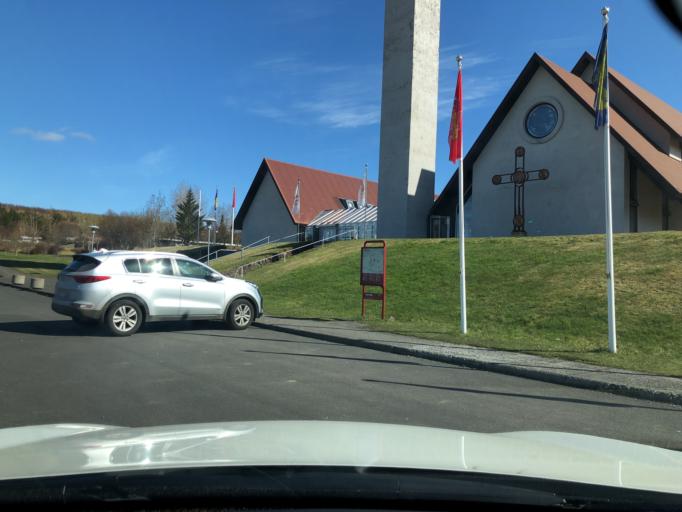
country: IS
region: West
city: Borgarnes
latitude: 64.6645
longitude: -21.2942
